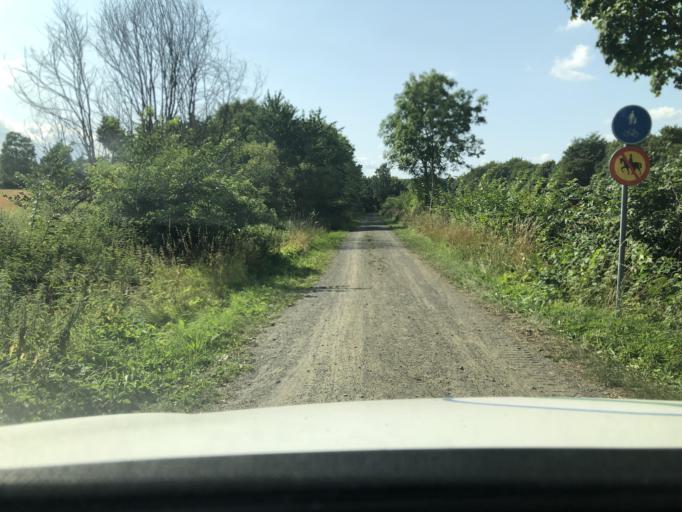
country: SE
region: Skane
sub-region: Kristianstads Kommun
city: Degeberga
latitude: 55.8016
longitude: 14.1455
